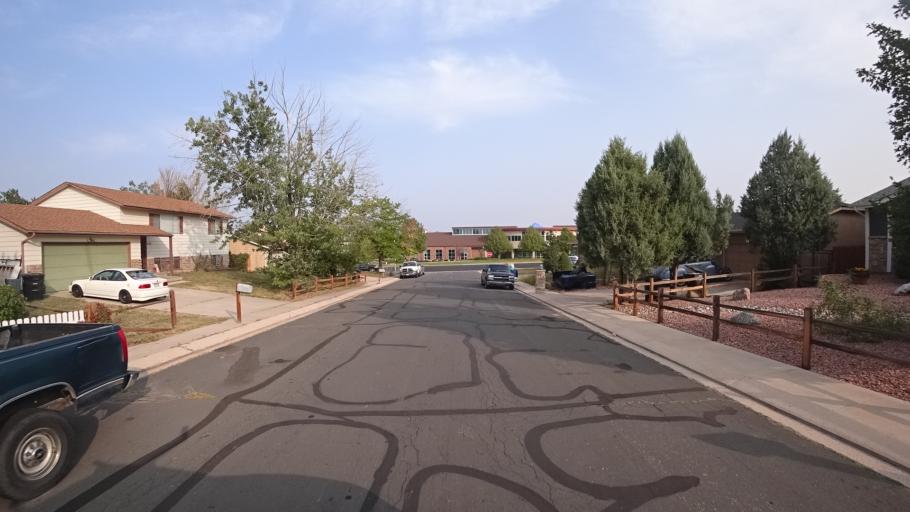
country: US
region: Colorado
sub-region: El Paso County
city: Stratmoor
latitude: 38.8014
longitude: -104.7493
